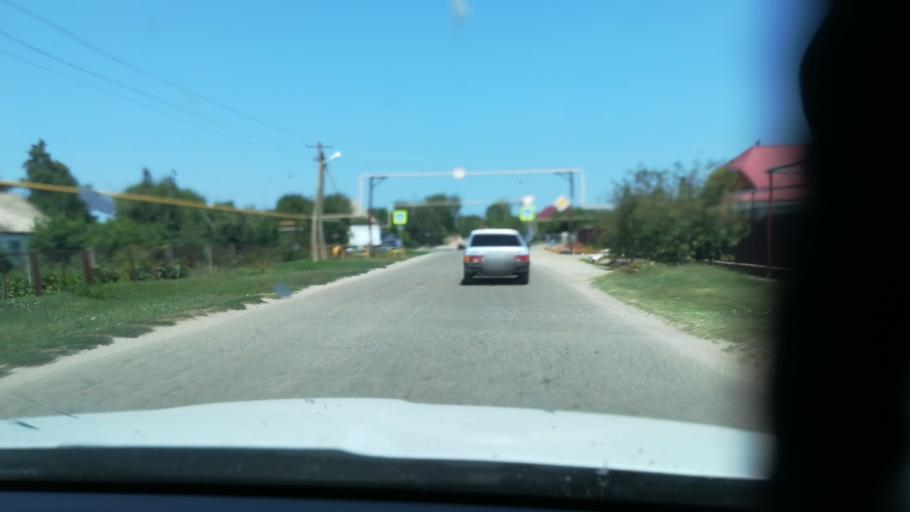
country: RU
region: Krasnodarskiy
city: Starotitarovskaya
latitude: 45.2163
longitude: 37.1423
